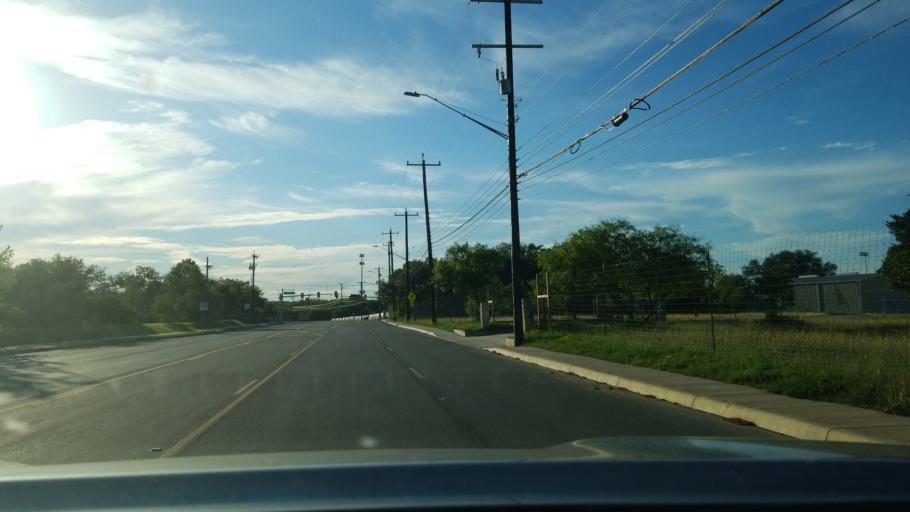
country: US
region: Texas
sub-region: Bexar County
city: Hollywood Park
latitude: 29.6180
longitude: -98.4565
